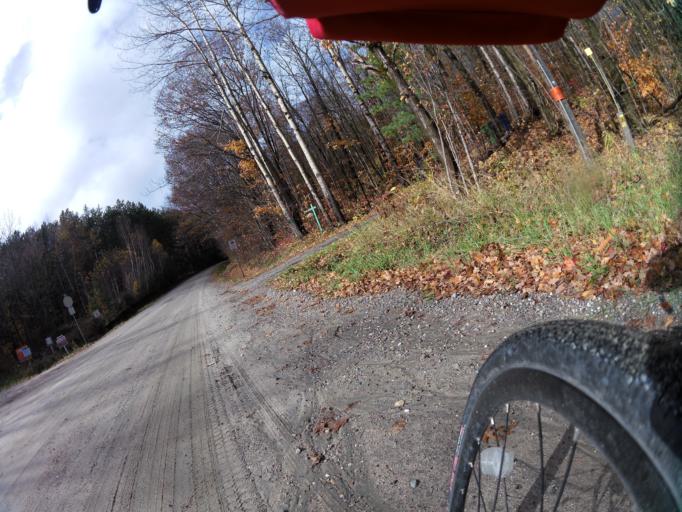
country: CA
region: Quebec
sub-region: Outaouais
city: Wakefield
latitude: 45.6969
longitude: -76.0196
